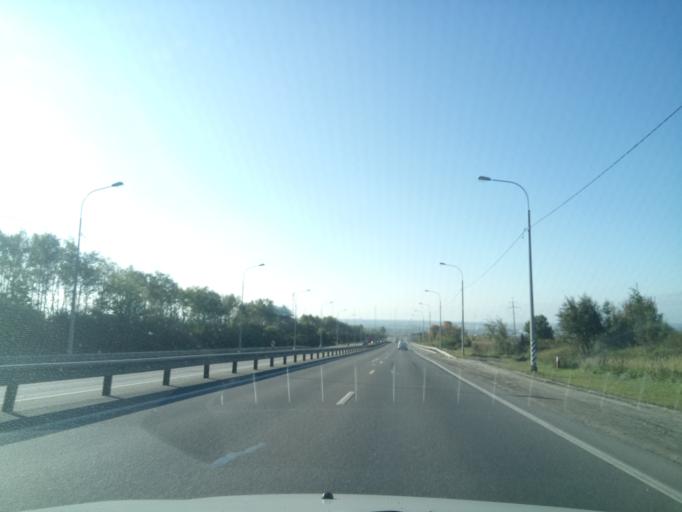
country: RU
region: Nizjnij Novgorod
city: Nizhniy Novgorod
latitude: 56.2019
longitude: 43.9256
